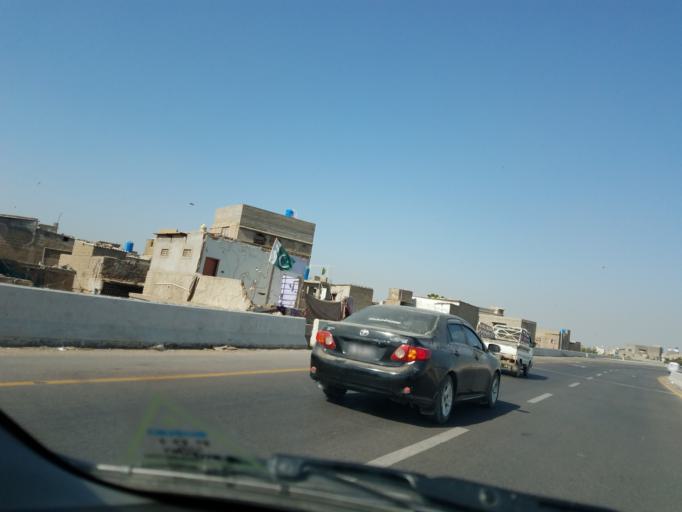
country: PK
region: Sindh
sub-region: Karachi District
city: Karachi
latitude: 24.8820
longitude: 67.0180
